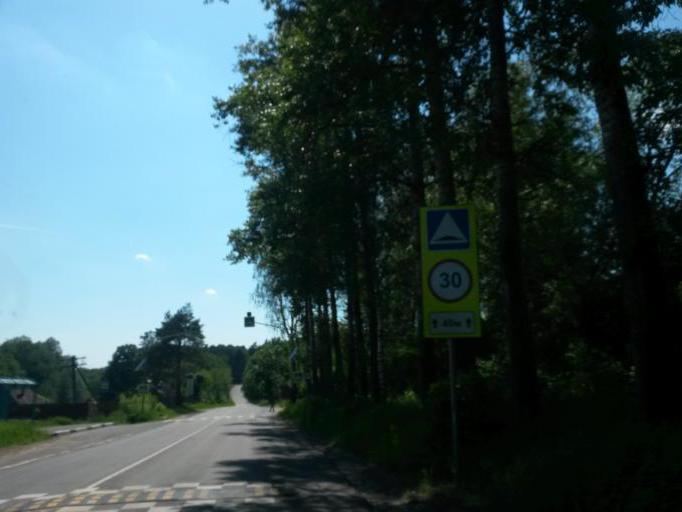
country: RU
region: Moskovskaya
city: Danki
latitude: 54.9109
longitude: 37.5591
